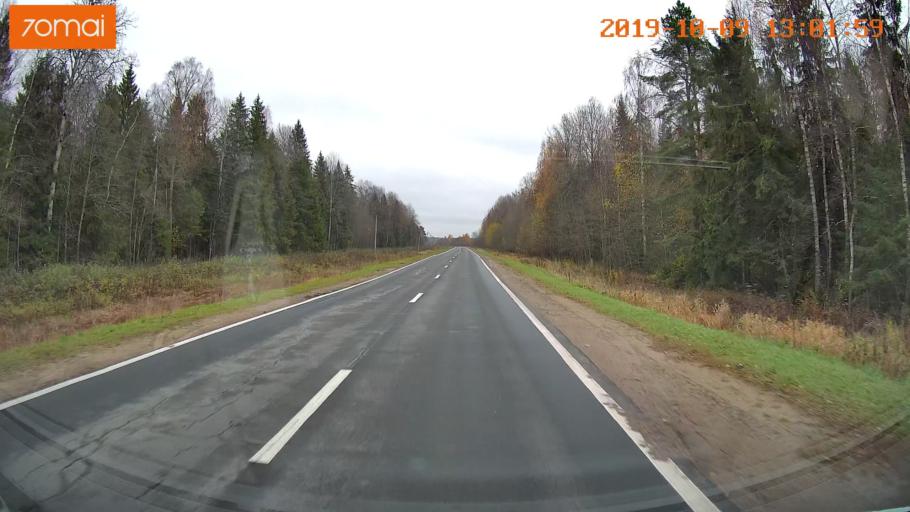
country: RU
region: Jaroslavl
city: Prechistoye
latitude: 58.3647
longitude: 40.4931
